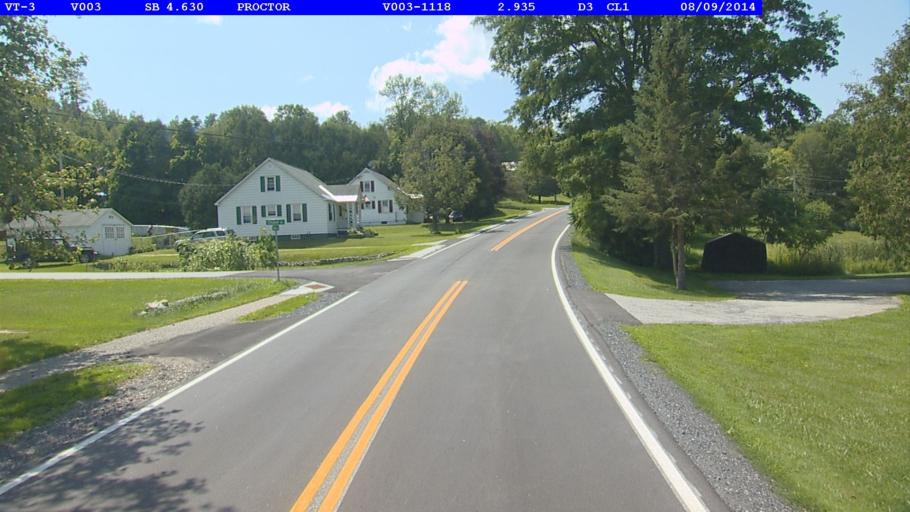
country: US
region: Vermont
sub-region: Rutland County
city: West Rutland
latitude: 43.6633
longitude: -73.0276
